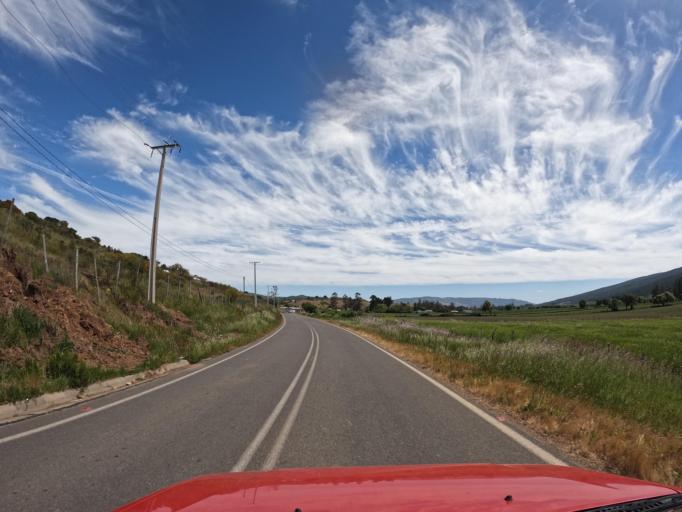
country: CL
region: Maule
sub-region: Provincia de Talca
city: Constitucion
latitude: -34.9997
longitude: -72.0248
